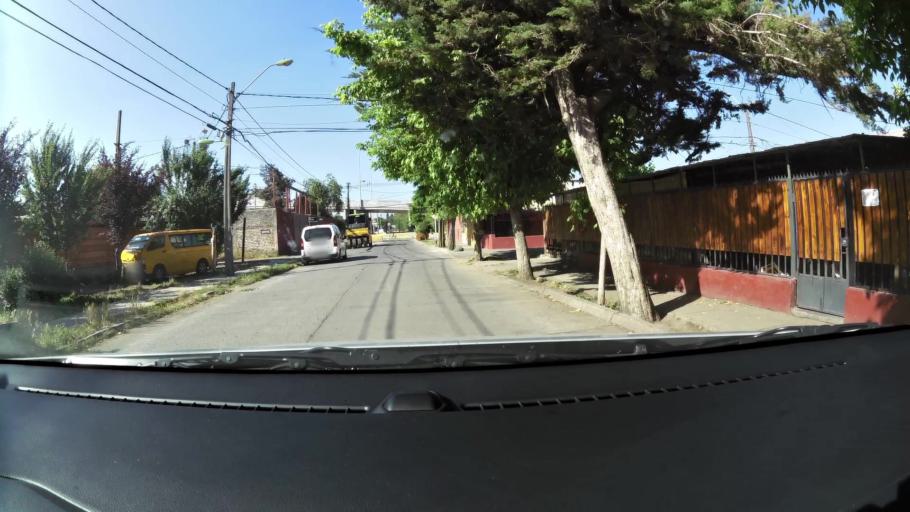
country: CL
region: Santiago Metropolitan
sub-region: Provincia de Maipo
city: San Bernardo
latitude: -33.5727
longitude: -70.6995
